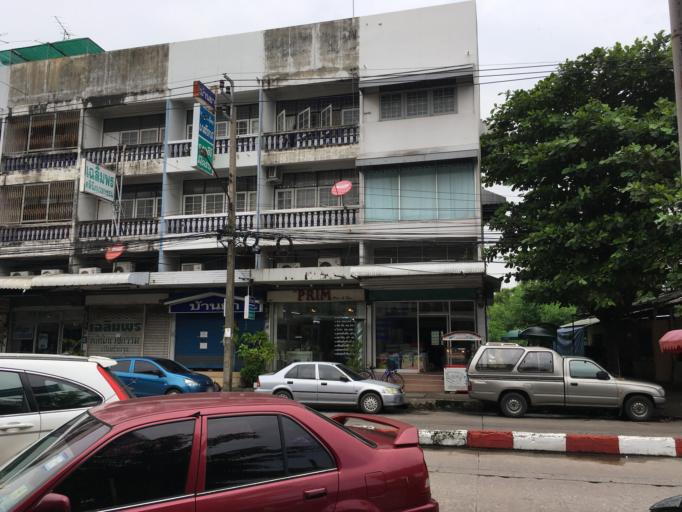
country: TH
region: Bangkok
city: Bueng Kum
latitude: 13.7863
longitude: 100.6752
